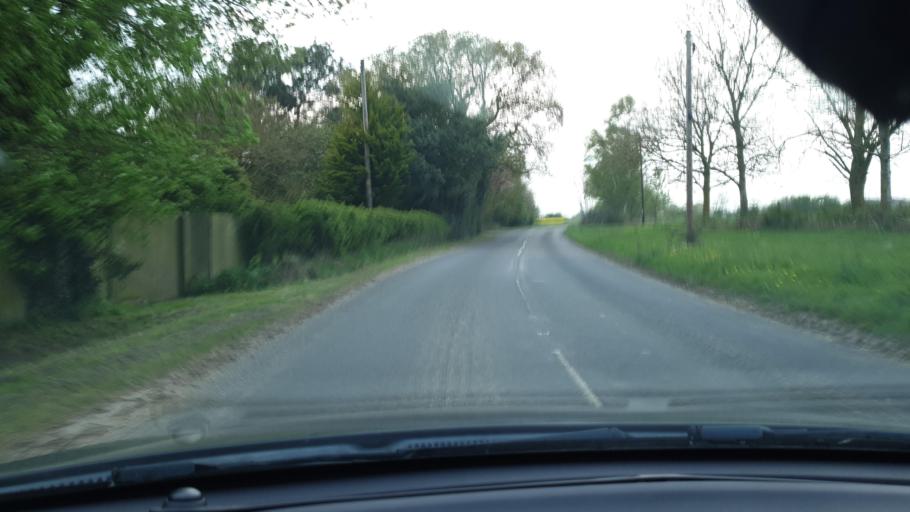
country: GB
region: England
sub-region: Essex
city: Mistley
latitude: 51.9051
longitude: 1.1062
